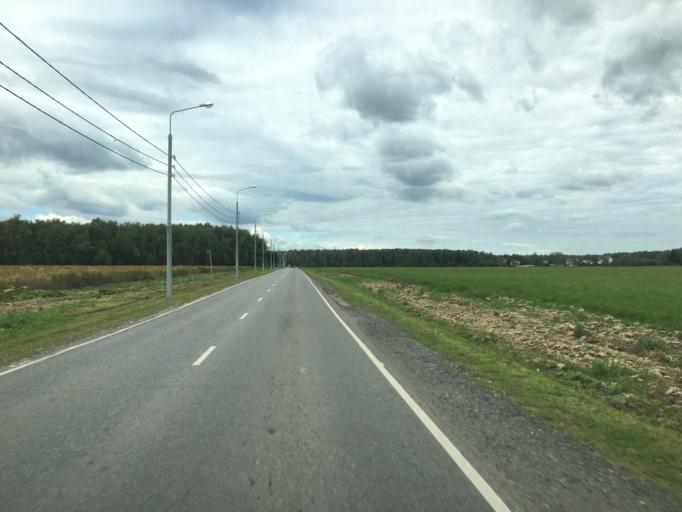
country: RU
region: Moskovskaya
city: Vatutinki
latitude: 55.4941
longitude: 37.3958
